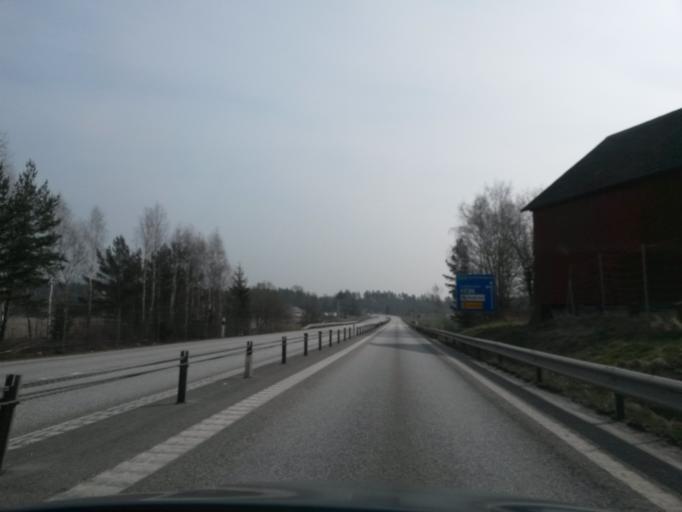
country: SE
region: Vaestra Goetaland
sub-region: Toreboda Kommun
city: Toereboda
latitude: 58.7988
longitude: 14.0480
